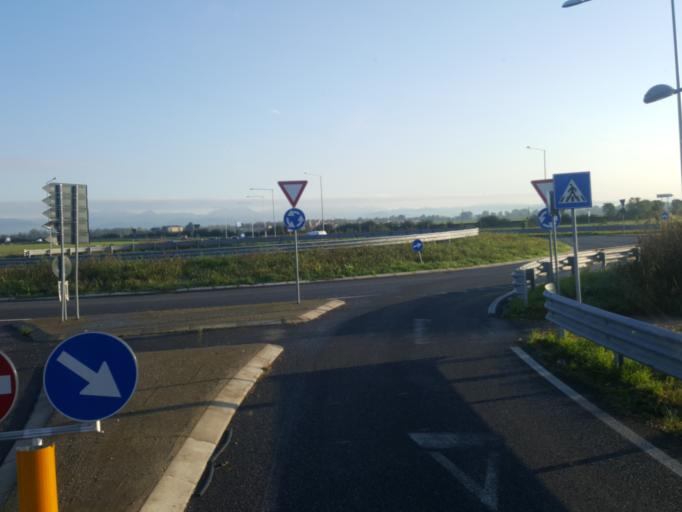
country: IT
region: Lombardy
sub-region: Provincia di Bergamo
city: Morengo
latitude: 45.5439
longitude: 9.7030
